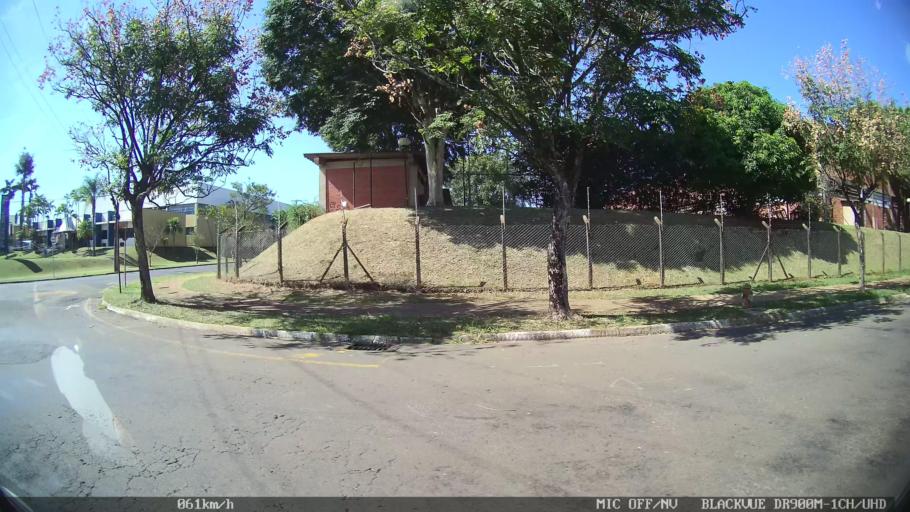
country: BR
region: Sao Paulo
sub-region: Franca
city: Franca
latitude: -20.5500
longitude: -47.4369
